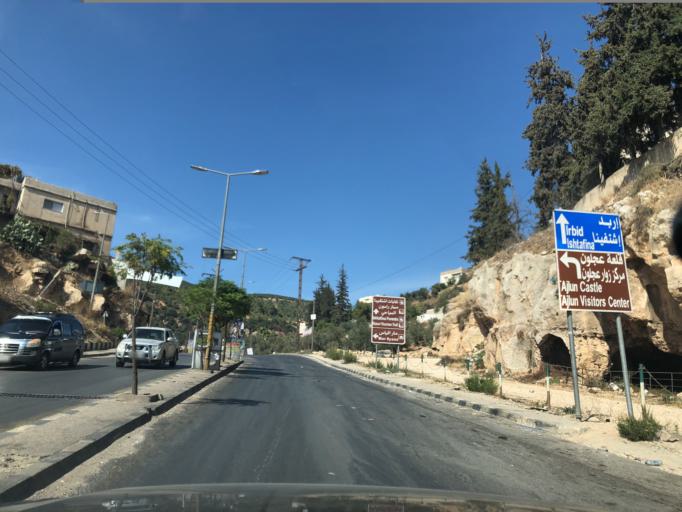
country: JO
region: Ajlun
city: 'Ajlun
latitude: 32.3338
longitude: 35.7519
